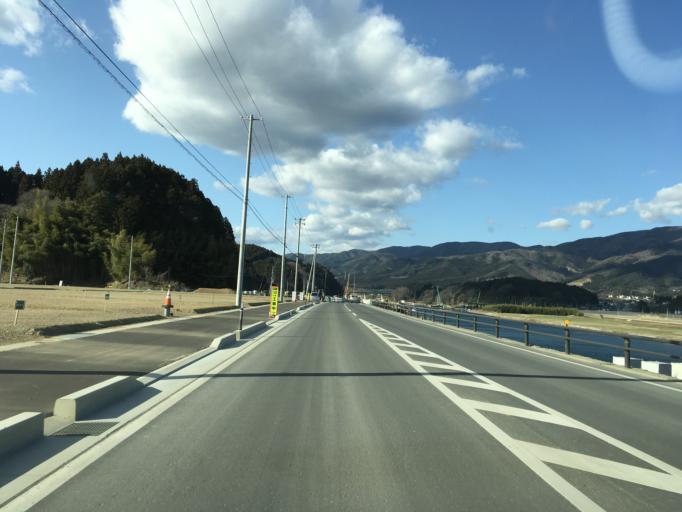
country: JP
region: Iwate
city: Ofunato
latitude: 39.0106
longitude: 141.6162
